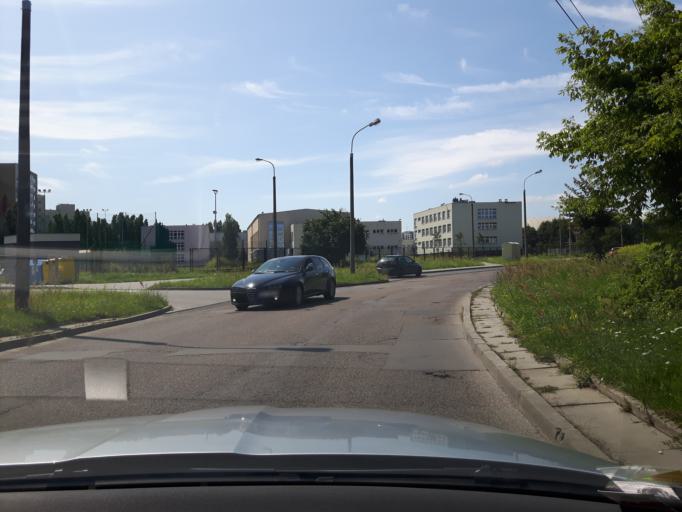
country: PL
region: Pomeranian Voivodeship
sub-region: Sopot
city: Sopot
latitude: 54.4034
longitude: 18.6051
